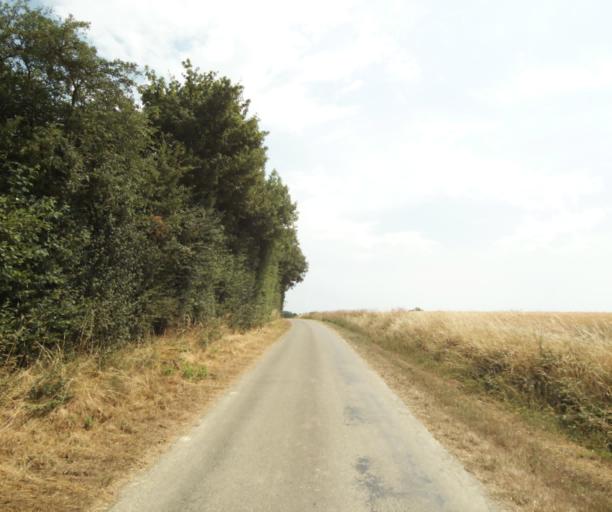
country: FR
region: Centre
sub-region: Departement d'Eure-et-Loir
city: La Bazoche-Gouet
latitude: 48.1847
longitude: 0.9850
